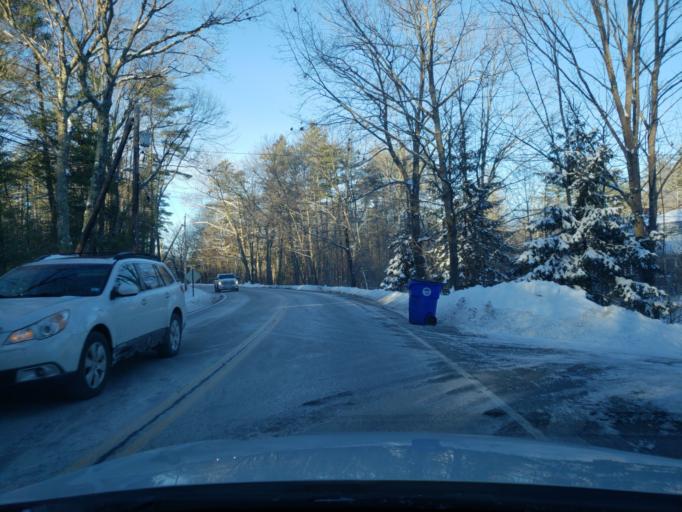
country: US
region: New Hampshire
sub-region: Hillsborough County
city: Goffstown
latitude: 43.0176
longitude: -71.6200
